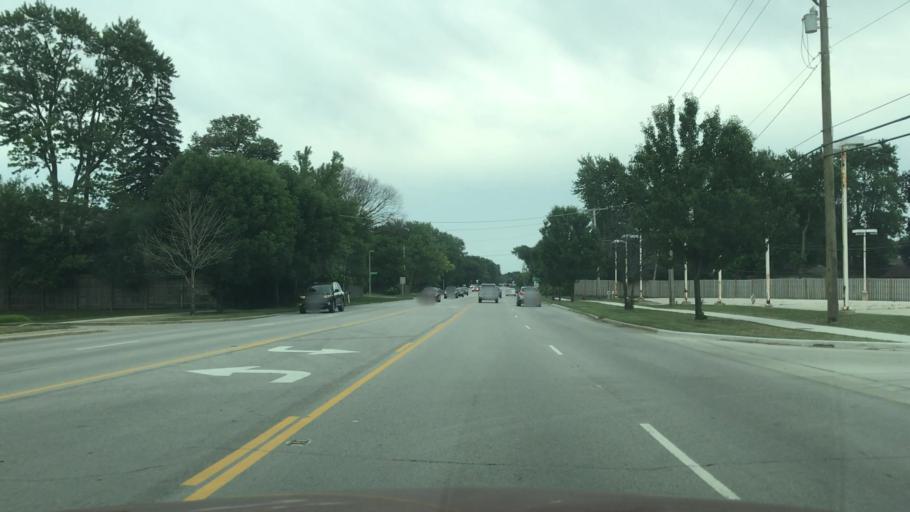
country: US
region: Illinois
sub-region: Cook County
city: Mount Prospect
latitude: 42.0651
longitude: -87.9184
